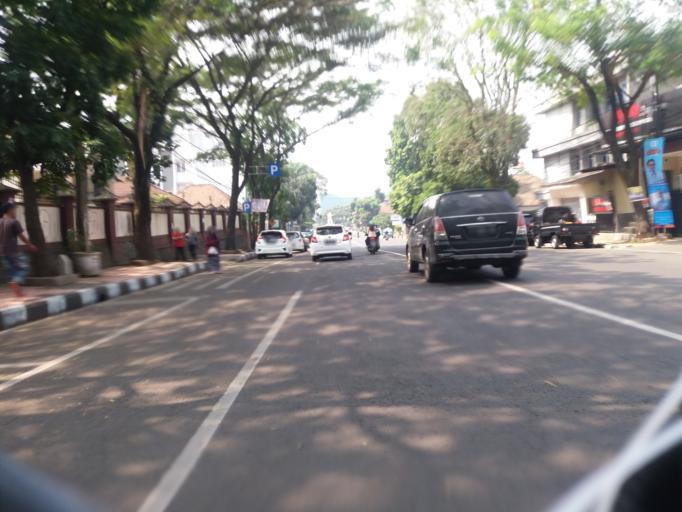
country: ID
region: West Java
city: Bandung
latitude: -6.9070
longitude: 107.6022
